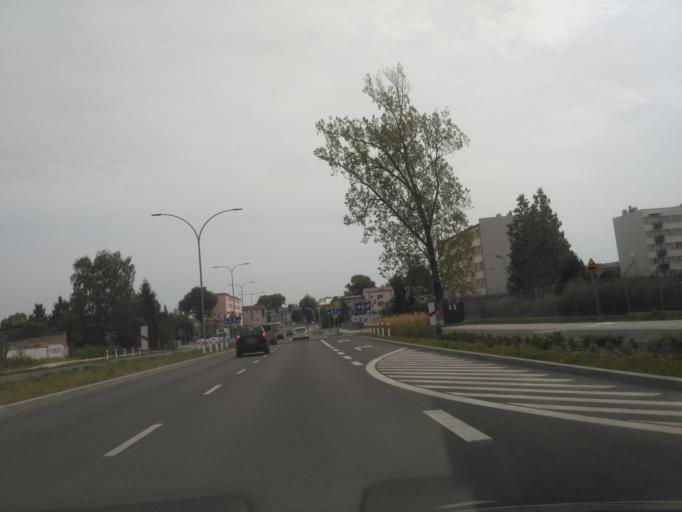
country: PL
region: Lublin Voivodeship
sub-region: Powiat lubelski
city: Lublin
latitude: 51.2232
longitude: 22.5690
